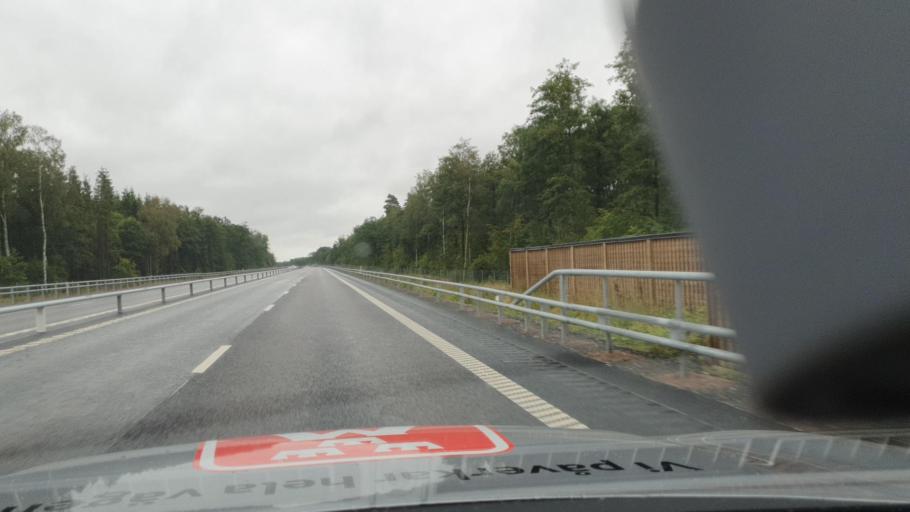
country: SE
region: Skane
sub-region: Kristianstads Kommun
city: Onnestad
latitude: 55.9610
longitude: 13.9679
